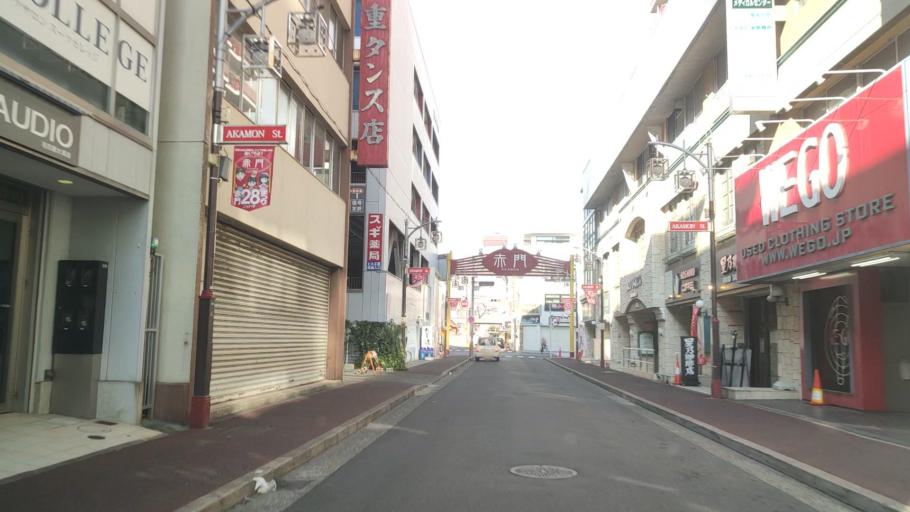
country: JP
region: Aichi
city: Nagoya-shi
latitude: 35.1605
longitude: 136.9026
